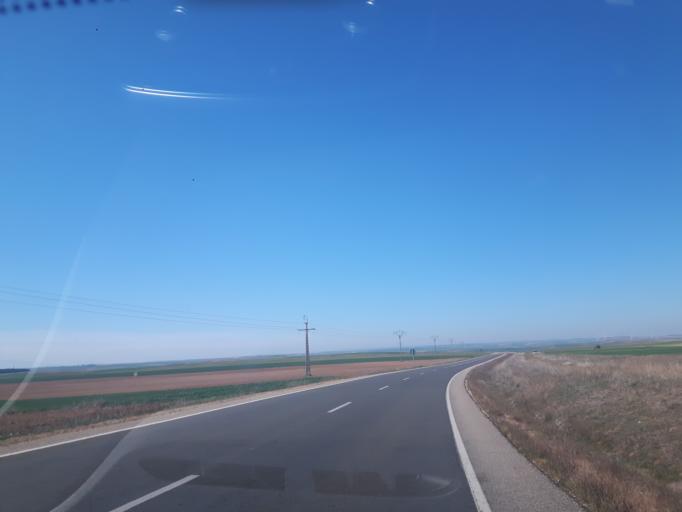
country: ES
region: Castille and Leon
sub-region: Provincia de Salamanca
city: Coca de Alba
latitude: 40.8782
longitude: -5.3354
